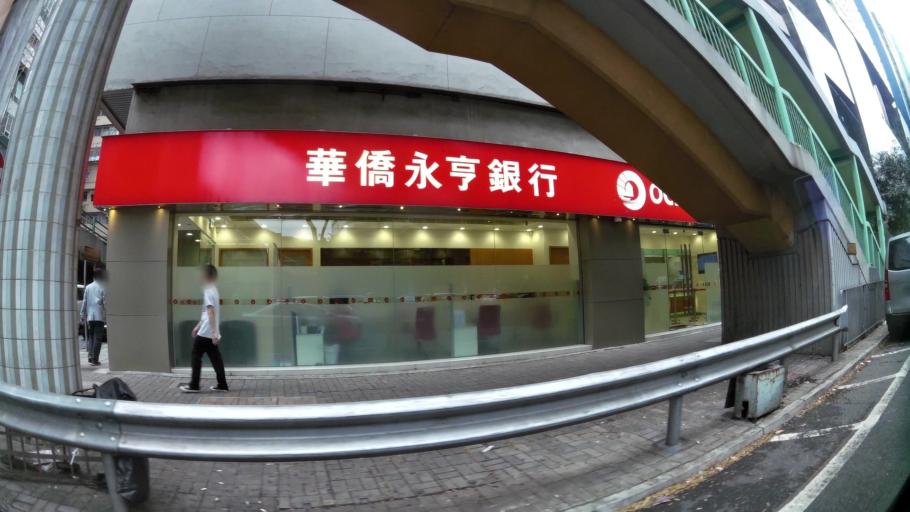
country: HK
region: Wanchai
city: Wan Chai
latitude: 22.2790
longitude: 114.1747
